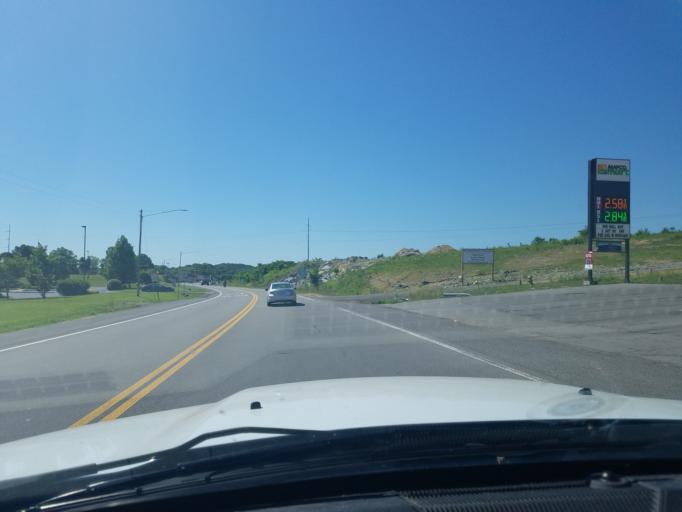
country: US
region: Tennessee
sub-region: Sumner County
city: Westmoreland
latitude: 36.5568
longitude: -86.2397
